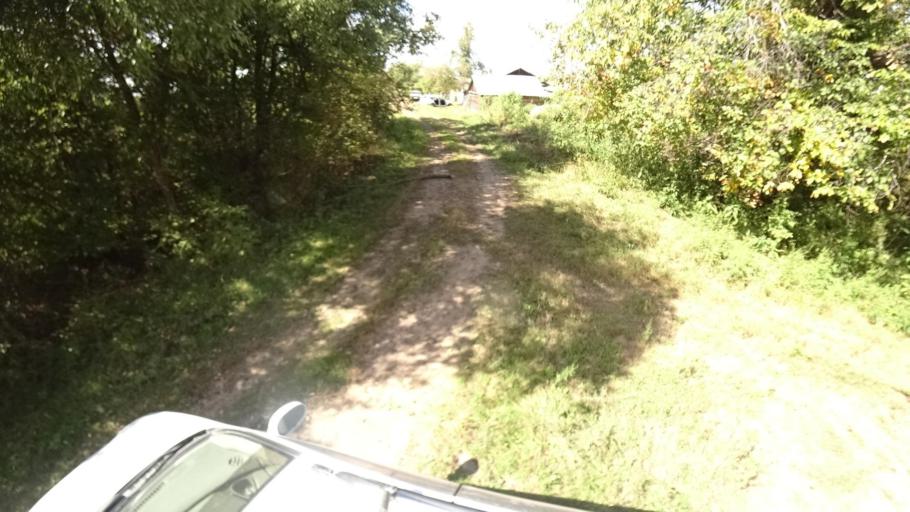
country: RU
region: Primorskiy
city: Yakovlevka
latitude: 44.4290
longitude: 133.5738
